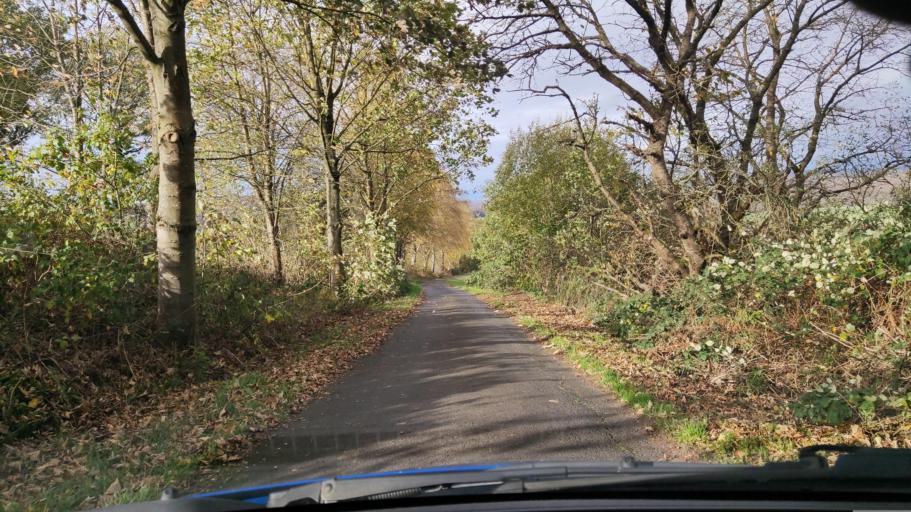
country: DE
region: Lower Saxony
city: Bodenfelde
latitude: 51.6177
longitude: 9.5712
